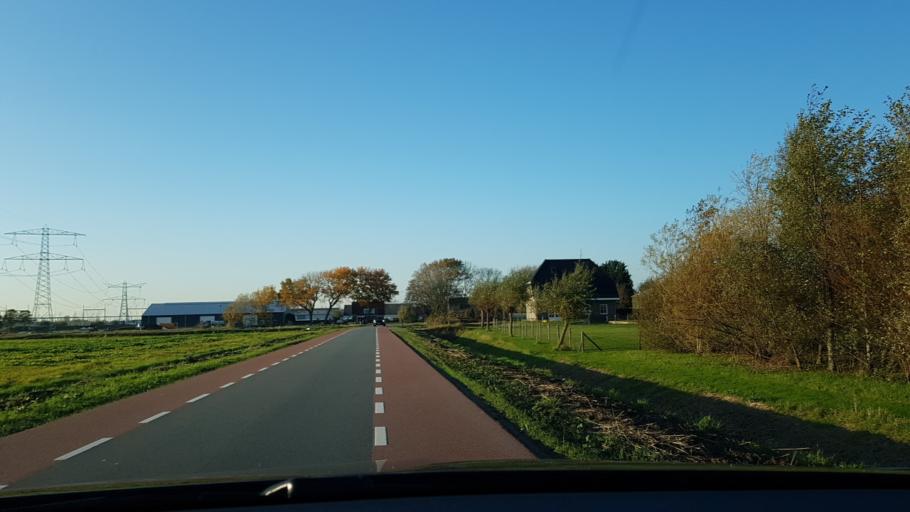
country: NL
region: North Holland
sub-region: Gemeente Beverwijk
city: Beverwijk
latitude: 52.4706
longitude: 4.6906
